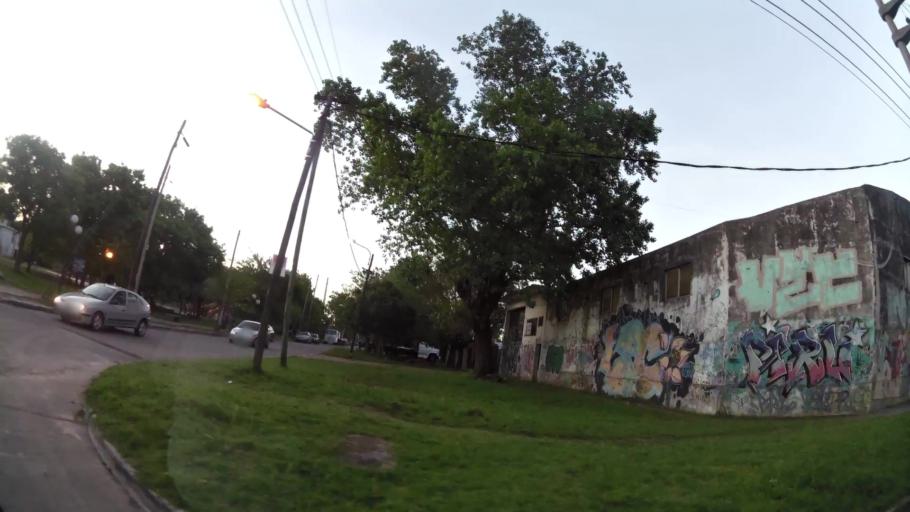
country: AR
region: Buenos Aires
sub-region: Partido de Quilmes
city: Quilmes
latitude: -34.7723
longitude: -58.2055
